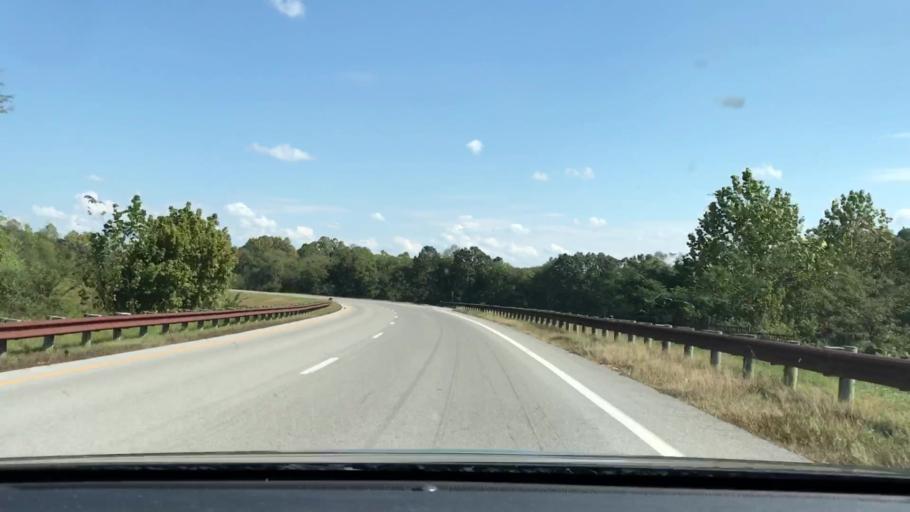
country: US
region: Kentucky
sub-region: Trigg County
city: Cadiz
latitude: 36.7847
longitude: -88.0174
